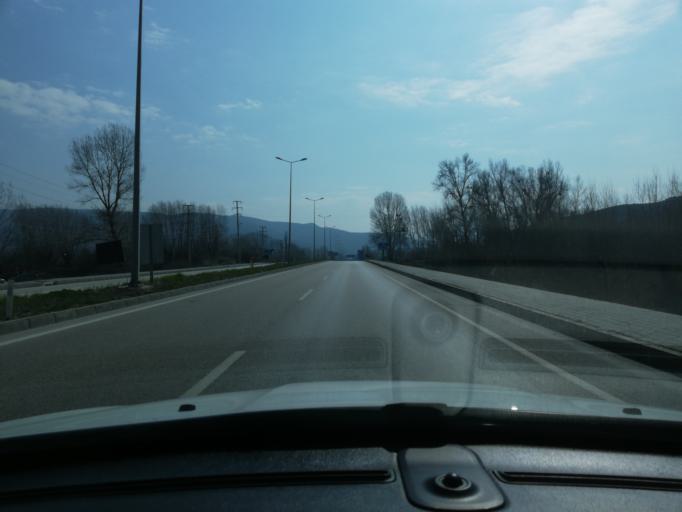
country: TR
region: Cankiri
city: Ilgaz
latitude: 40.9076
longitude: 33.6379
